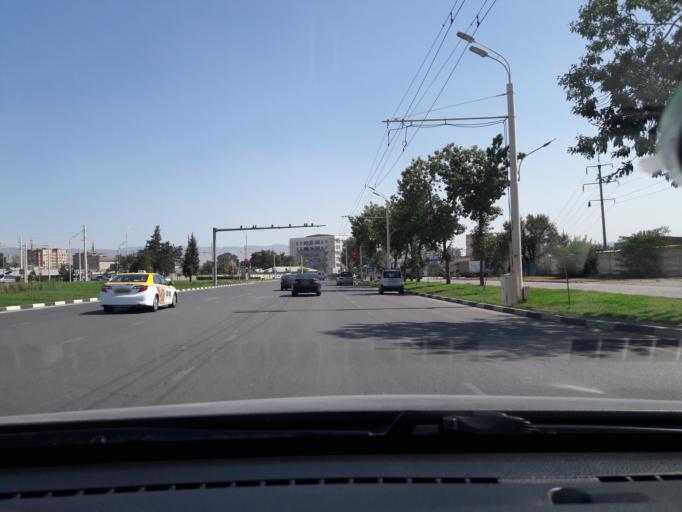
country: TJ
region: Dushanbe
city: Dushanbe
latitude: 38.5382
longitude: 68.7409
